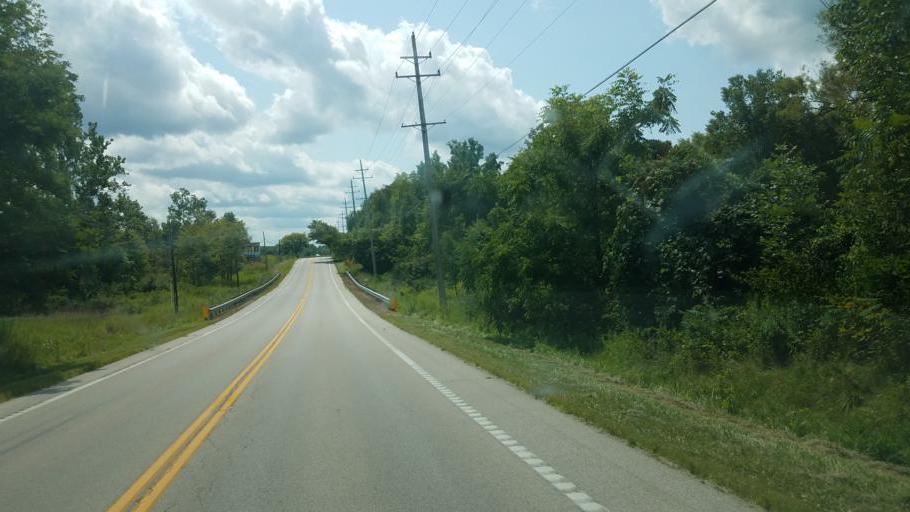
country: US
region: Ohio
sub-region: Ashtabula County
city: Roaming Shores
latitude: 41.6812
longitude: -80.8555
